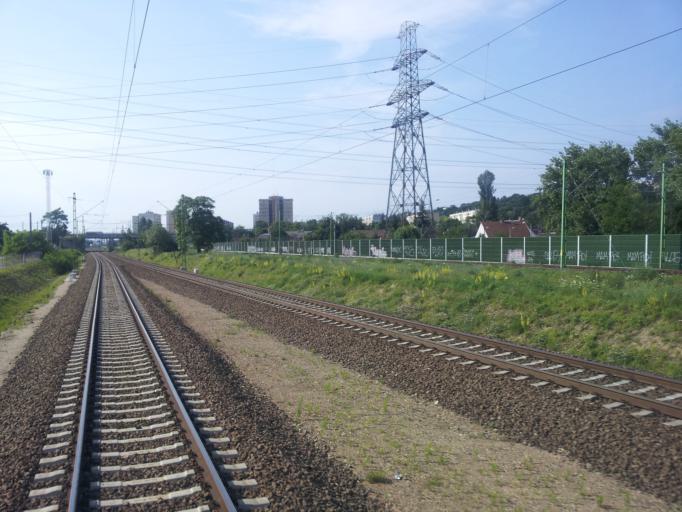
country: HU
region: Budapest
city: Budapest XXII. keruelet
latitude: 47.4387
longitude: 19.0356
